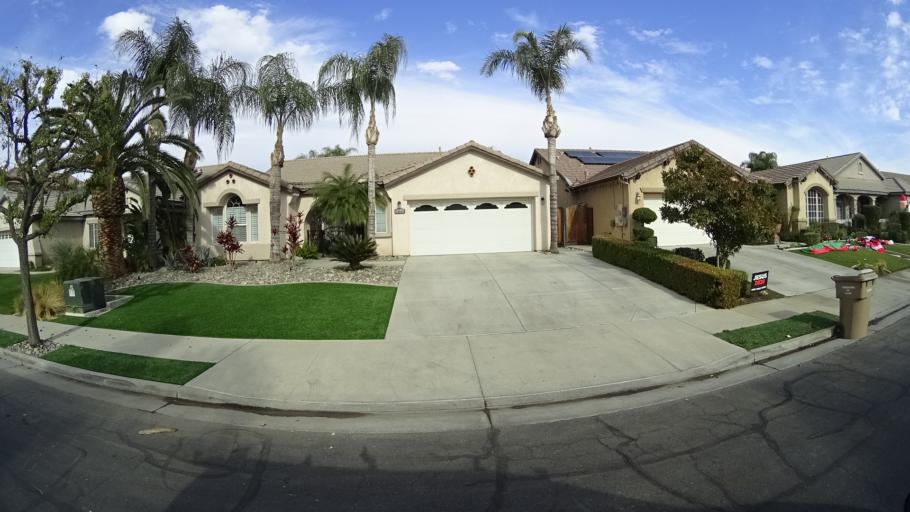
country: US
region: California
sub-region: Kern County
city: Greenacres
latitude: 35.4150
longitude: -119.1145
